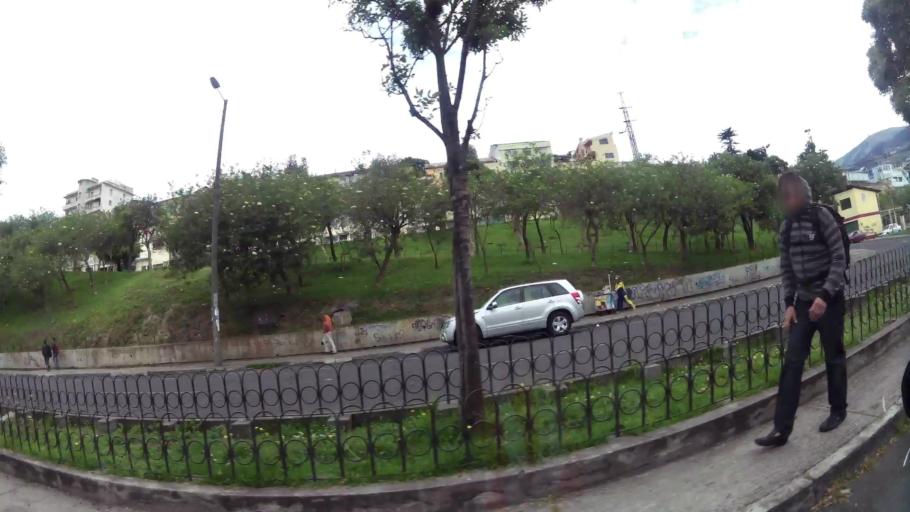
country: EC
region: Pichincha
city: Quito
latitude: -0.2263
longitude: -78.5087
